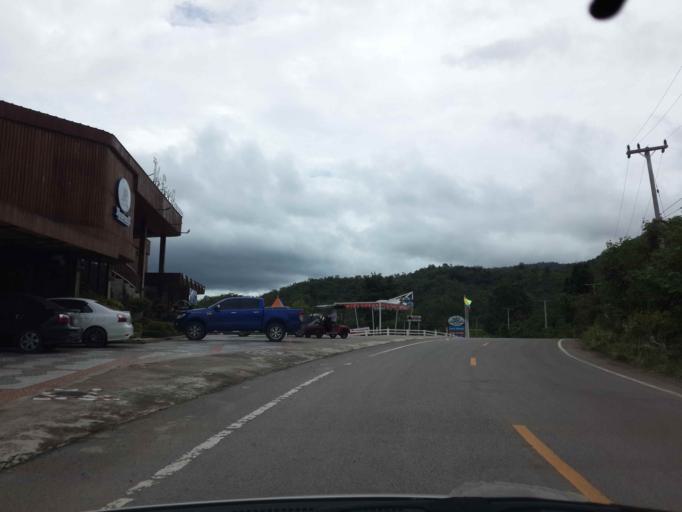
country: TH
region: Ratchaburi
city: Suan Phueng
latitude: 13.7011
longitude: 99.1984
